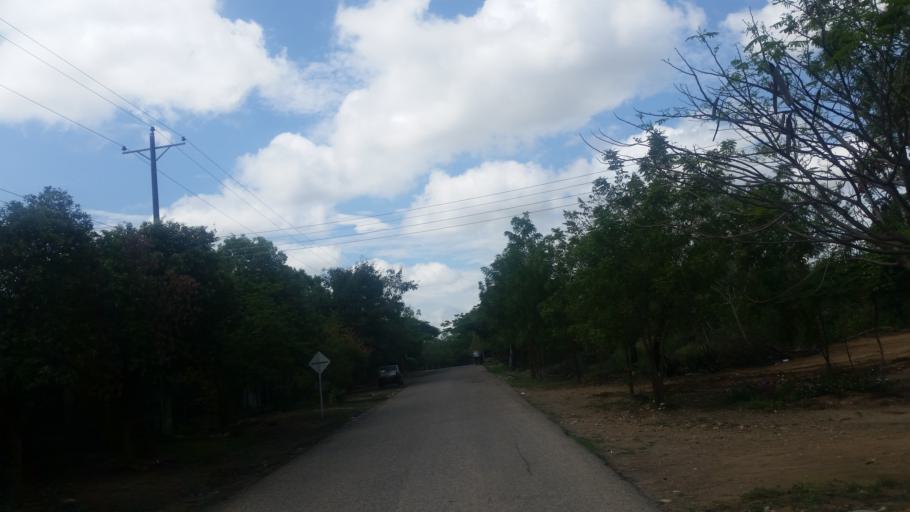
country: CO
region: Huila
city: Villavieja
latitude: 3.1867
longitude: -75.2186
